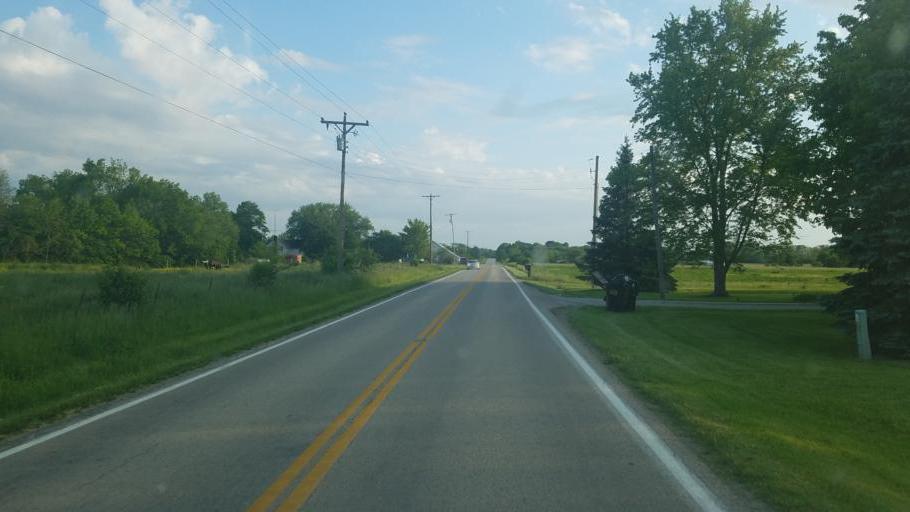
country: US
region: Ohio
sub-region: Highland County
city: Leesburg
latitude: 39.3671
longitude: -83.5928
